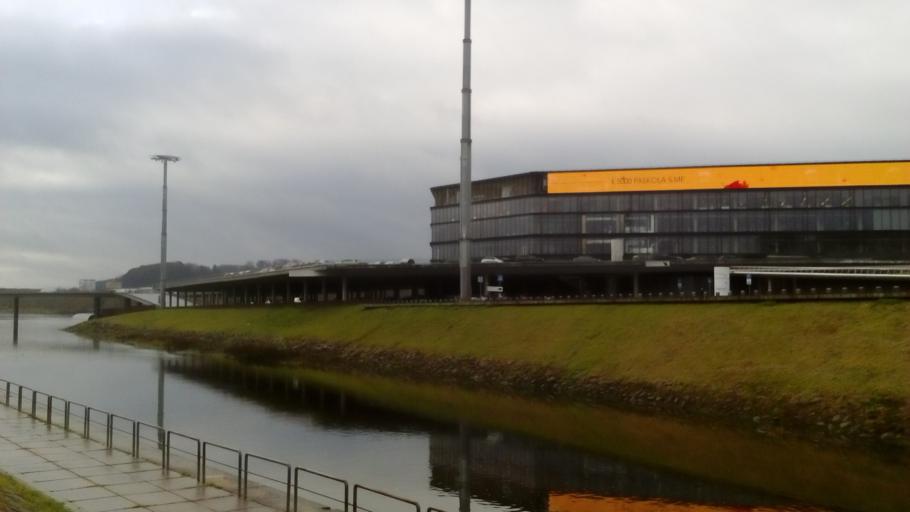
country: LT
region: Kauno apskritis
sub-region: Kaunas
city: Kaunas
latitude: 54.8922
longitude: 23.9160
